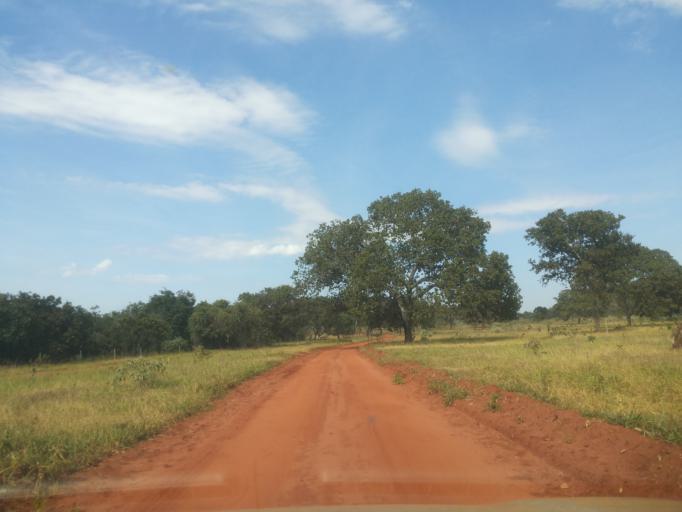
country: BR
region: Minas Gerais
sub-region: Ituiutaba
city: Ituiutaba
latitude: -19.0658
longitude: -49.3644
